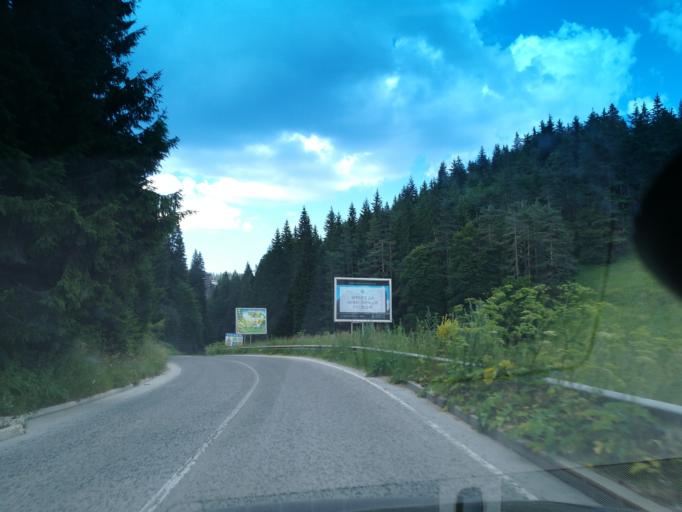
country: BG
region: Smolyan
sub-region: Obshtina Smolyan
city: Smolyan
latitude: 41.6518
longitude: 24.6956
